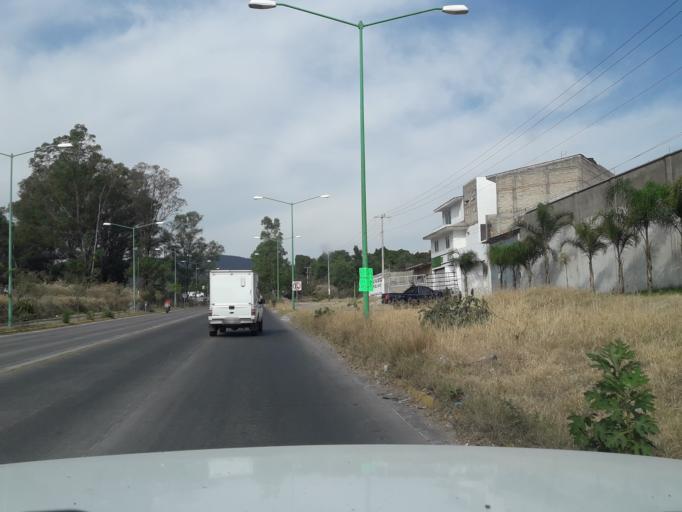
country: MX
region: Jalisco
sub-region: Tlajomulco de Zuniga
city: Palomar
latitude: 20.6211
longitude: -103.4754
